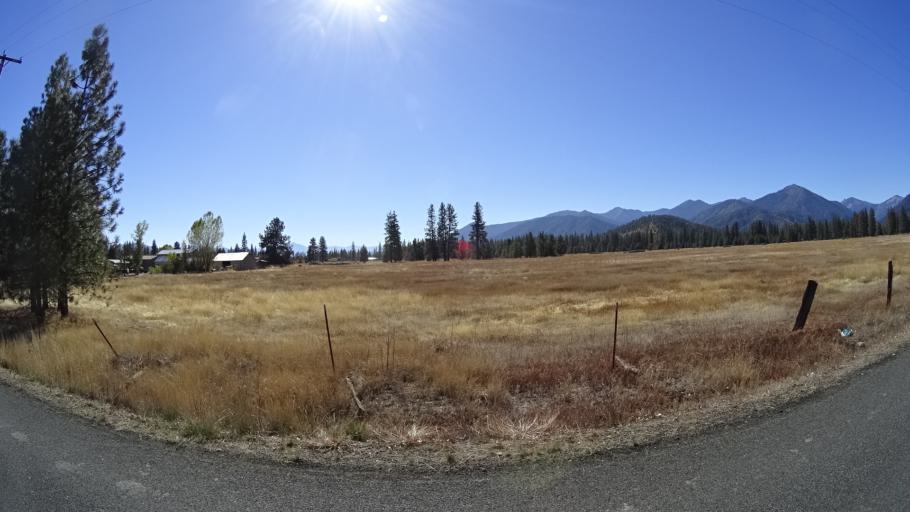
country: US
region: California
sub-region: Siskiyou County
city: Yreka
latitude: 41.5485
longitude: -122.9217
